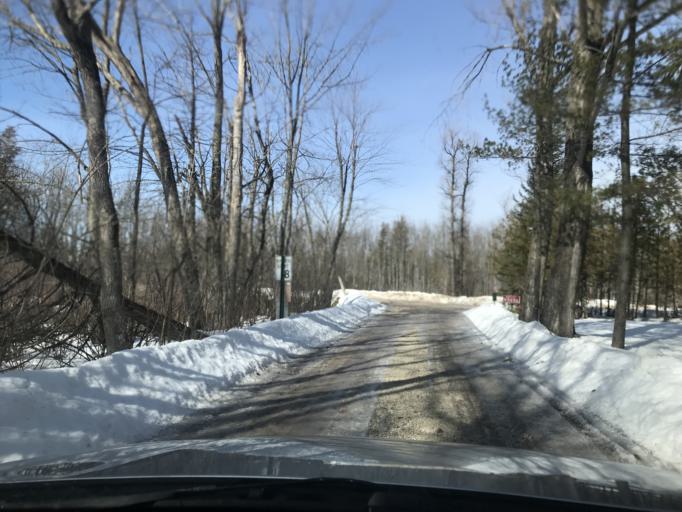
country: US
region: Wisconsin
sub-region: Marinette County
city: Peshtigo
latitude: 45.3004
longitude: -87.8236
